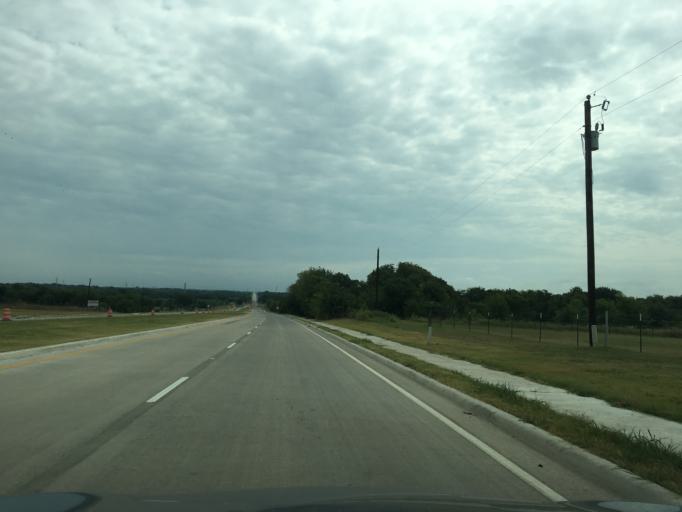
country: US
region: Texas
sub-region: Collin County
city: Anna
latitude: 33.3111
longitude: -96.5145
